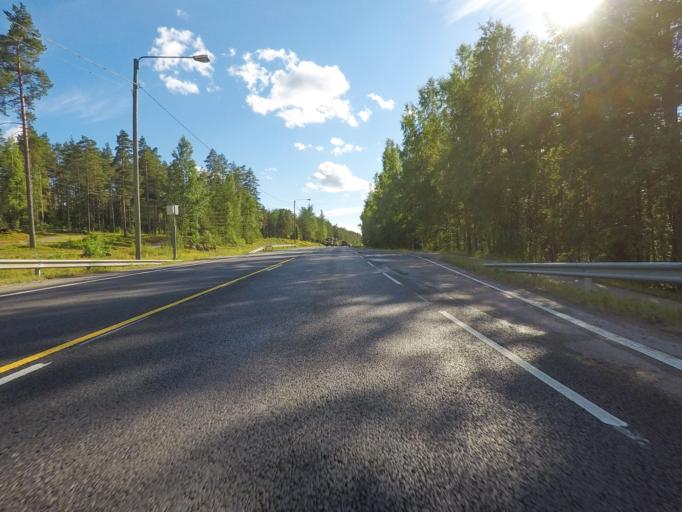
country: FI
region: Uusimaa
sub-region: Helsinki
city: Vihti
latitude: 60.3416
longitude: 24.3048
